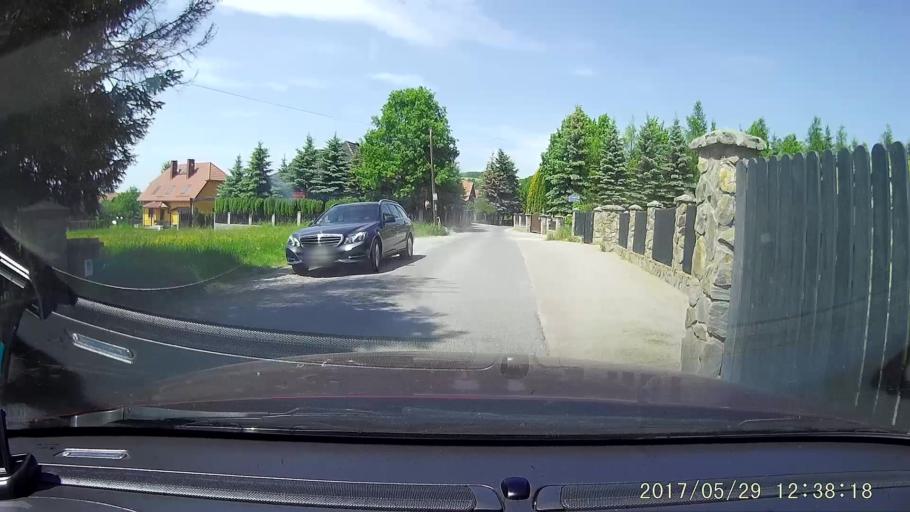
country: PL
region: Lower Silesian Voivodeship
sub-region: Powiat jeleniogorski
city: Jezow Sudecki
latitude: 50.9302
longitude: 15.7464
